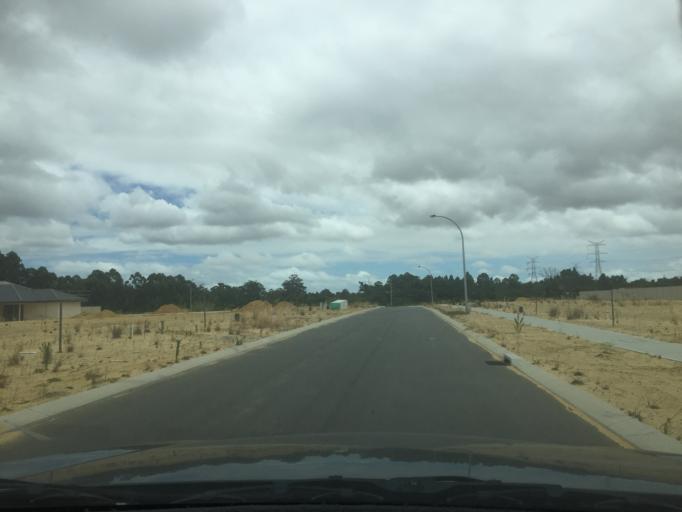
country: AU
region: Western Australia
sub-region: Armadale
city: Harrisdale
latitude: -32.1356
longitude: 115.9076
